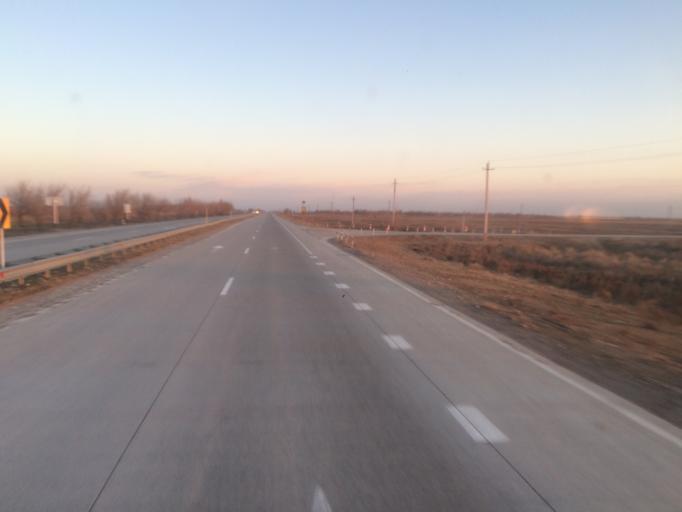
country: KZ
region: Ongtustik Qazaqstan
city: Bayaldyr
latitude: 43.0726
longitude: 68.6631
